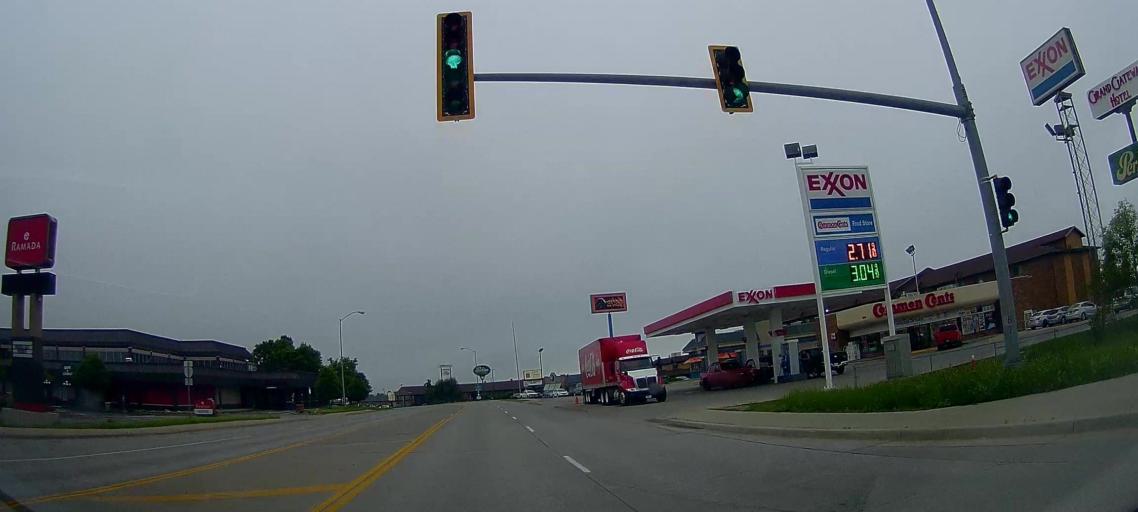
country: US
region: South Dakota
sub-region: Pennington County
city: Rapid City
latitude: 44.1033
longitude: -103.2036
